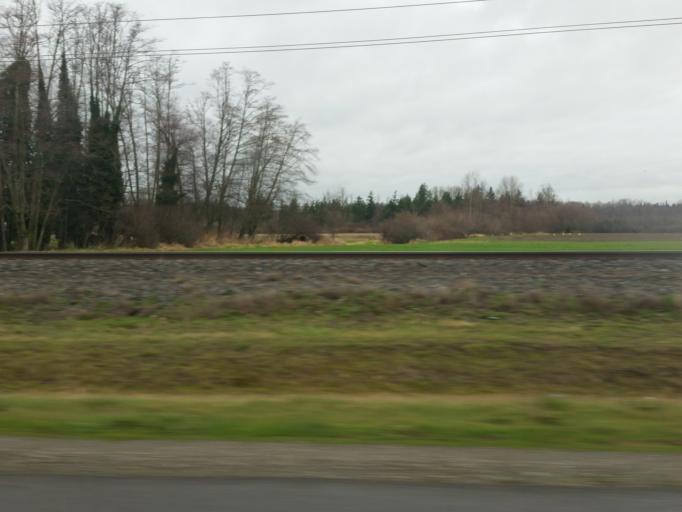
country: US
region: Washington
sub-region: Skagit County
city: Mount Vernon
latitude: 48.4500
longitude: -122.4159
